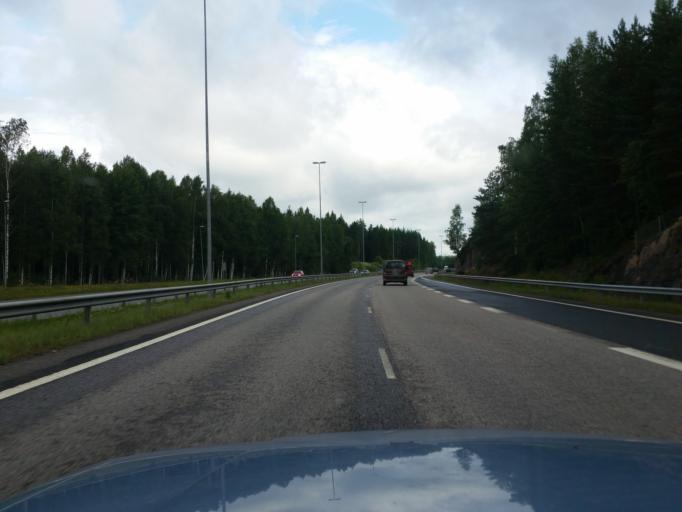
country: FI
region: Uusimaa
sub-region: Helsinki
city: Kirkkonummi
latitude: 60.2745
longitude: 24.4527
